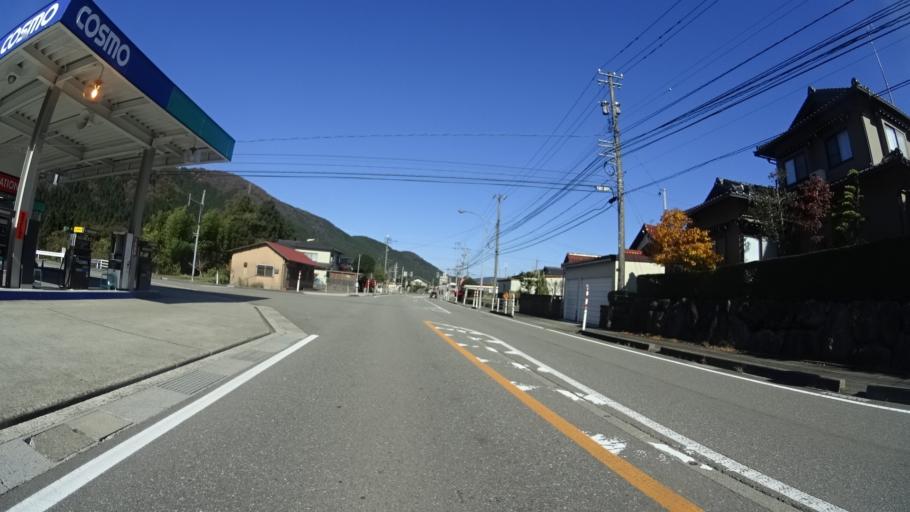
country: JP
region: Ishikawa
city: Tsurugi-asahimachi
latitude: 36.4112
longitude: 136.6324
